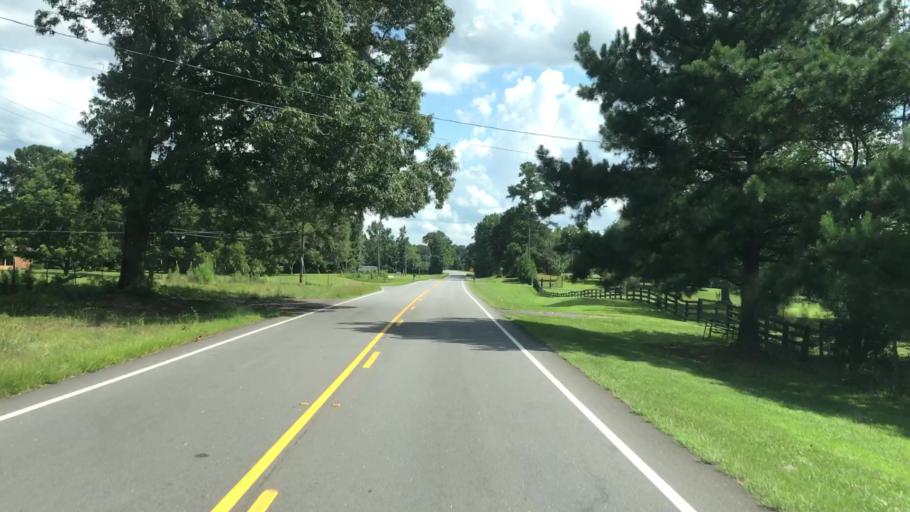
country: US
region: Georgia
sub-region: Newton County
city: Oxford
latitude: 33.6616
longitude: -83.8508
